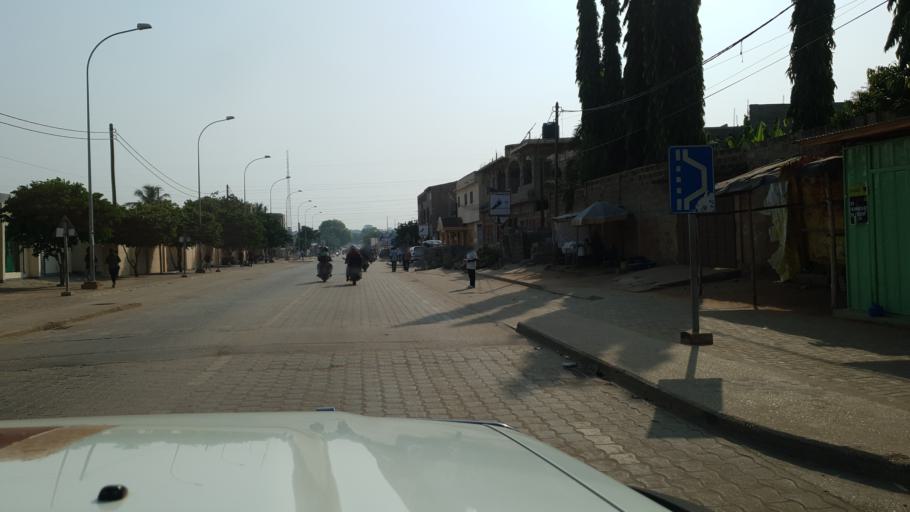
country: TG
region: Maritime
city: Lome
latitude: 6.1823
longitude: 1.2012
